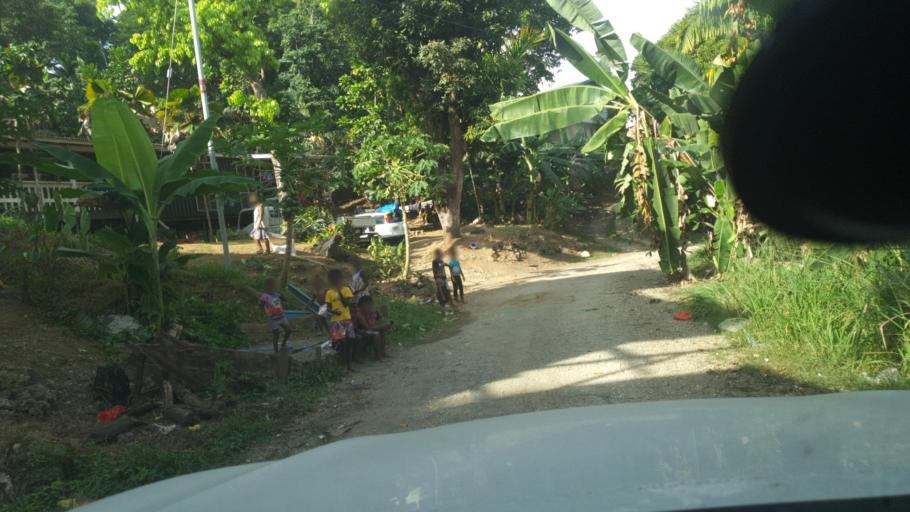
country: SB
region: Guadalcanal
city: Honiara
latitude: -9.4378
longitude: 159.9429
